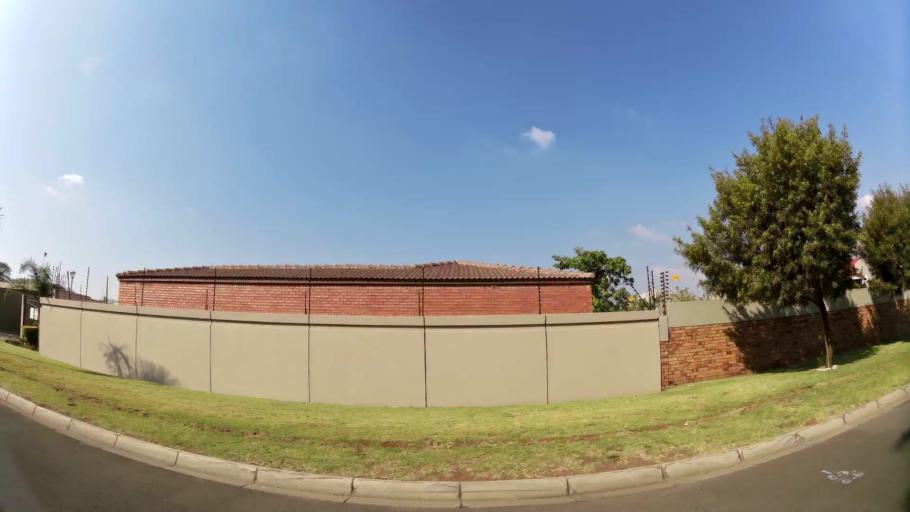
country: ZA
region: Gauteng
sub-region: Ekurhuleni Metropolitan Municipality
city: Boksburg
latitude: -26.1811
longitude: 28.2637
